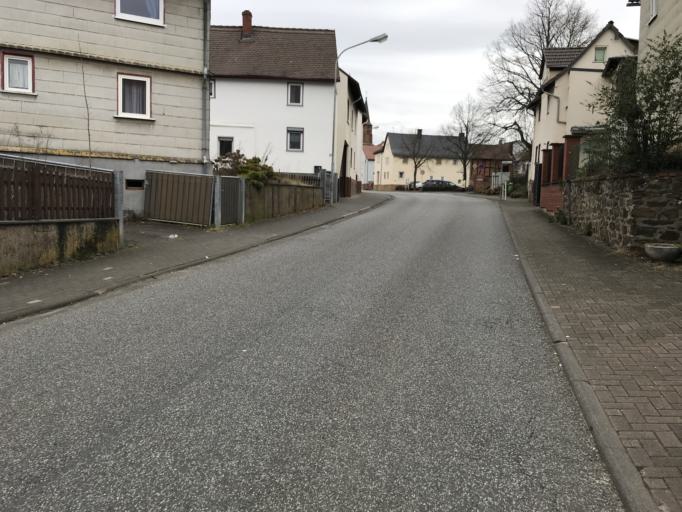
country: DE
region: Hesse
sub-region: Regierungsbezirk Giessen
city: Heuchelheim
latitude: 50.5892
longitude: 8.6138
